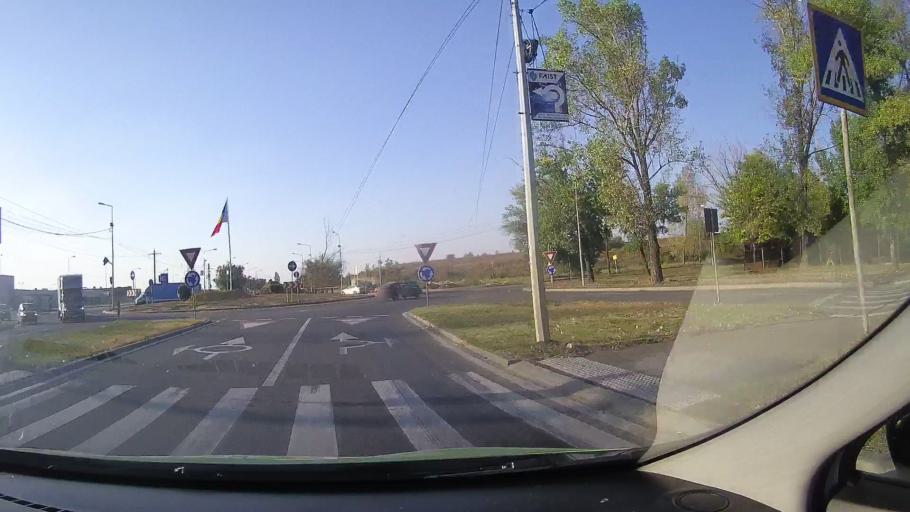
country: RO
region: Bihor
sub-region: Comuna Santandrei
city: Santandrei
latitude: 47.0879
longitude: 21.8783
